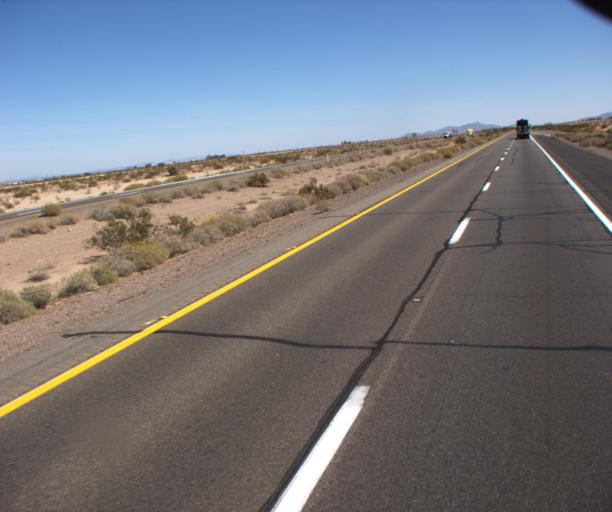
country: US
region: Arizona
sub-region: Yuma County
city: Wellton
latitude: 32.6817
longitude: -114.0206
